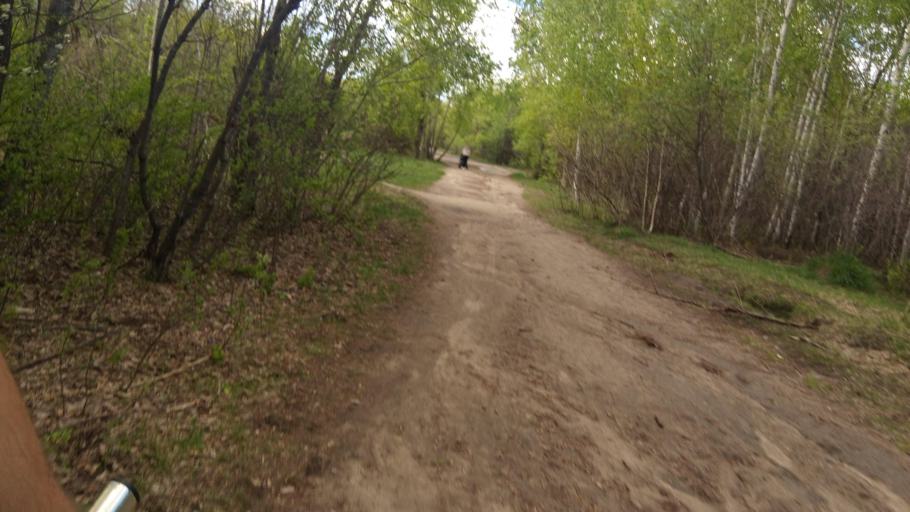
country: RU
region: Chelyabinsk
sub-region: Gorod Chelyabinsk
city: Chelyabinsk
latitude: 55.1683
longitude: 61.3414
